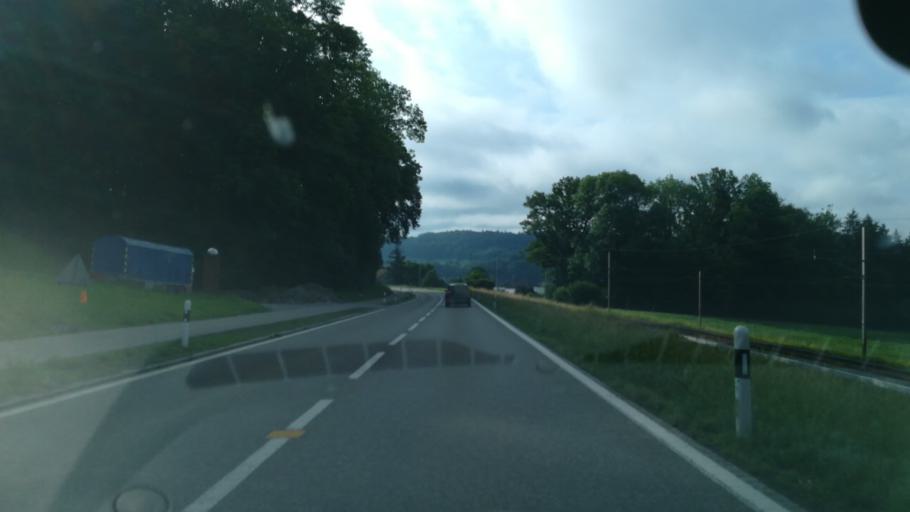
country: CH
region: Saint Gallen
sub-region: Wahlkreis Wil
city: Niederburen
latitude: 47.4985
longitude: 9.2188
